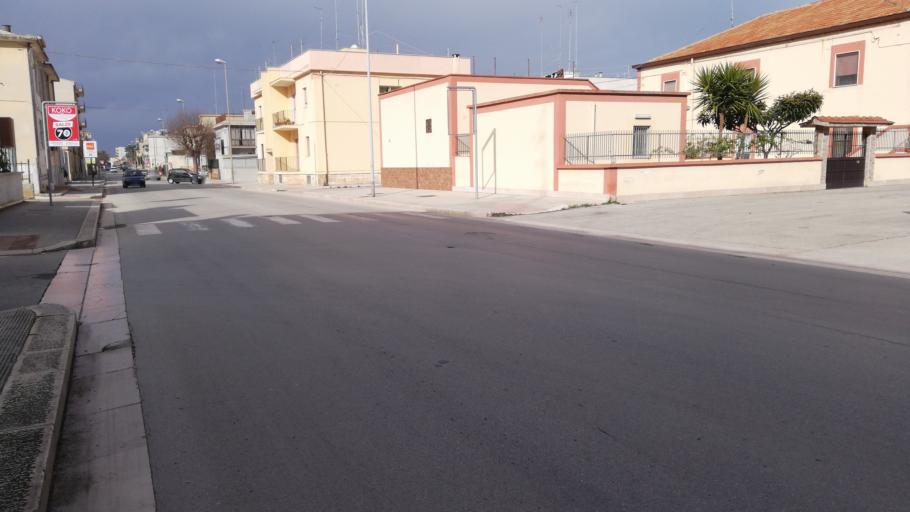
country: IT
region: Apulia
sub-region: Provincia di Barletta - Andria - Trani
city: Andria
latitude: 41.2388
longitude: 16.2993
